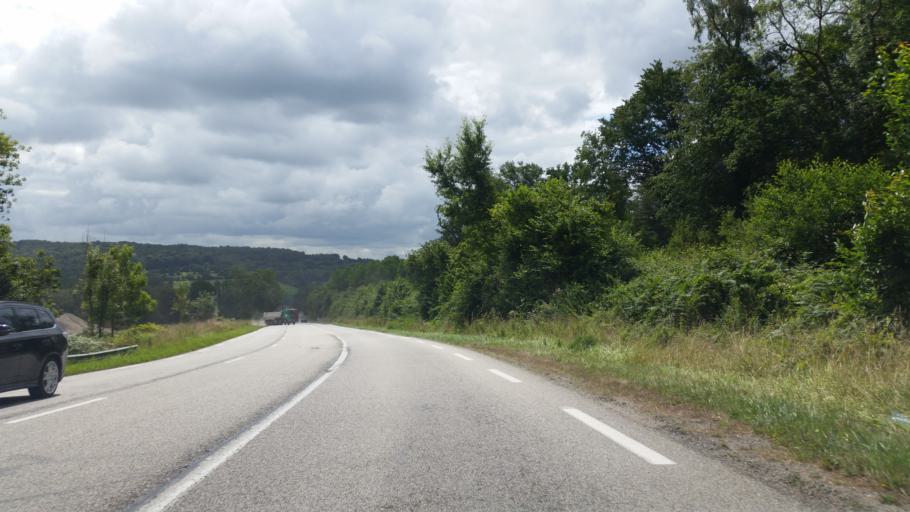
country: FR
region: Lower Normandy
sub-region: Departement du Calvados
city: Saint-Gatien-des-Bois
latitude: 49.3307
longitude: 0.2015
